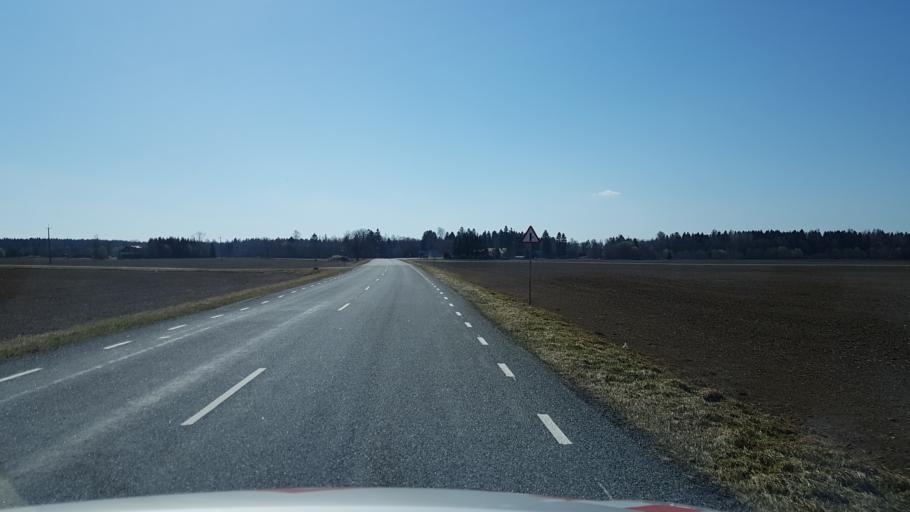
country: EE
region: Ida-Virumaa
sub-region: Kohtla-Nomme vald
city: Kohtla-Nomme
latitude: 59.3071
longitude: 27.2359
